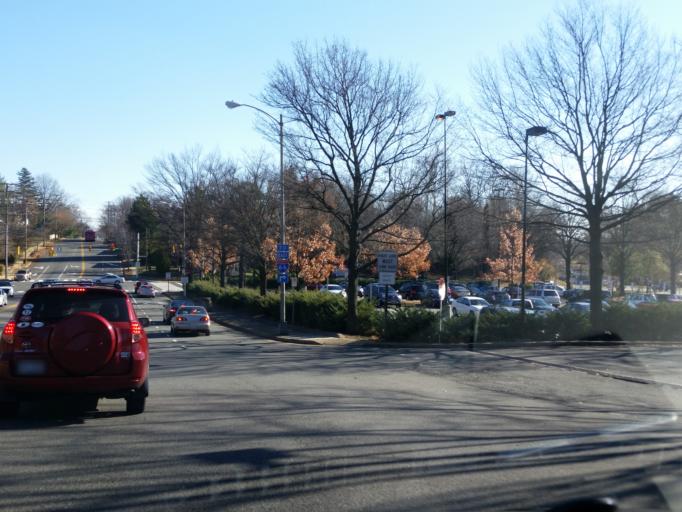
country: US
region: Virginia
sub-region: City of Falls Church
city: Falls Church
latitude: 38.8875
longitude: -77.1577
